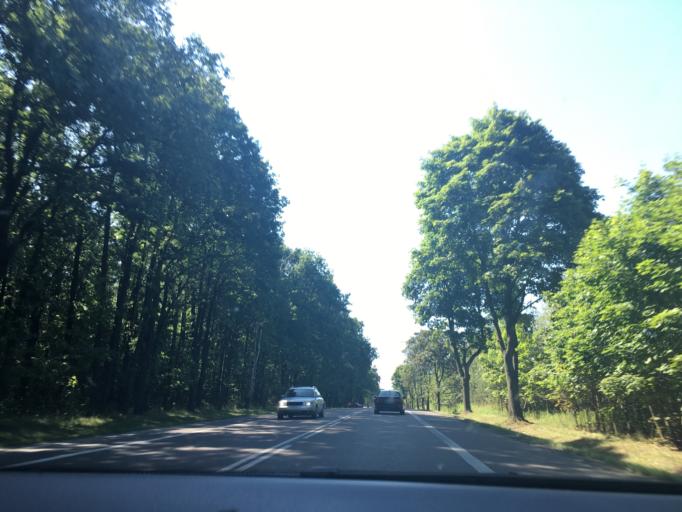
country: PL
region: Lublin Voivodeship
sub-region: Powiat lubelski
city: Niemce
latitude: 51.3951
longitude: 22.6365
